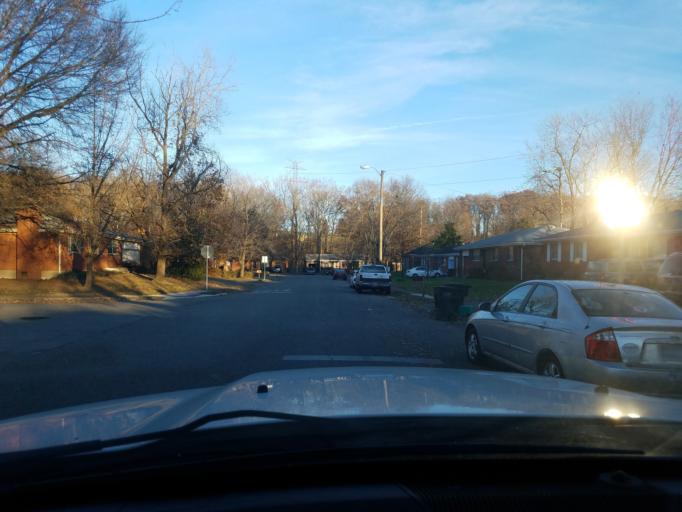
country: US
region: Indiana
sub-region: Floyd County
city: New Albany
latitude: 38.3196
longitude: -85.8340
